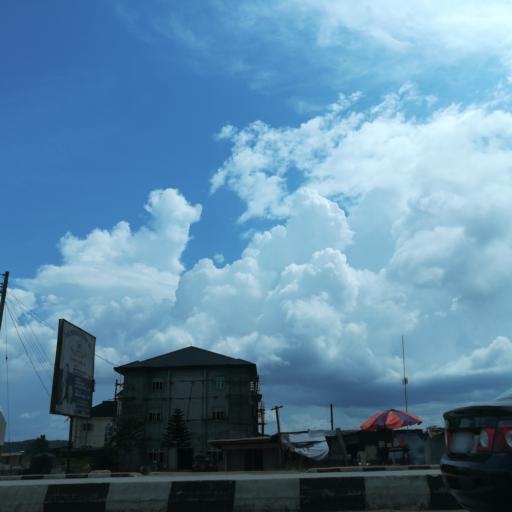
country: NG
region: Rivers
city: Port Harcourt
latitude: 4.8096
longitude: 7.0646
